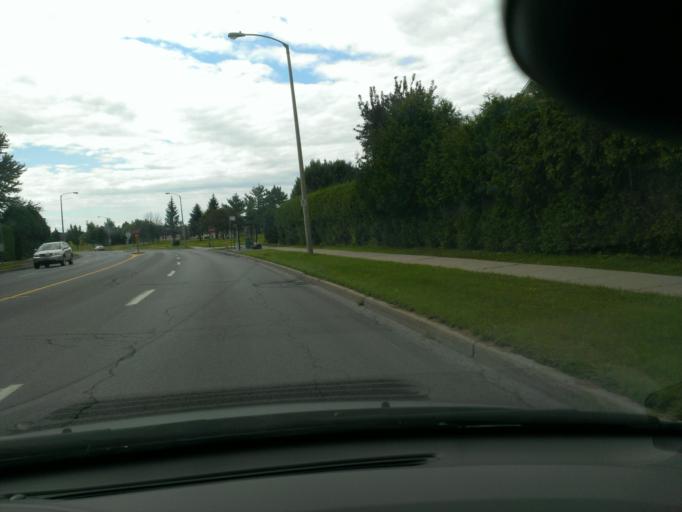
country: CA
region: Ontario
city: Clarence-Rockland
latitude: 45.4773
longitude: -75.4791
